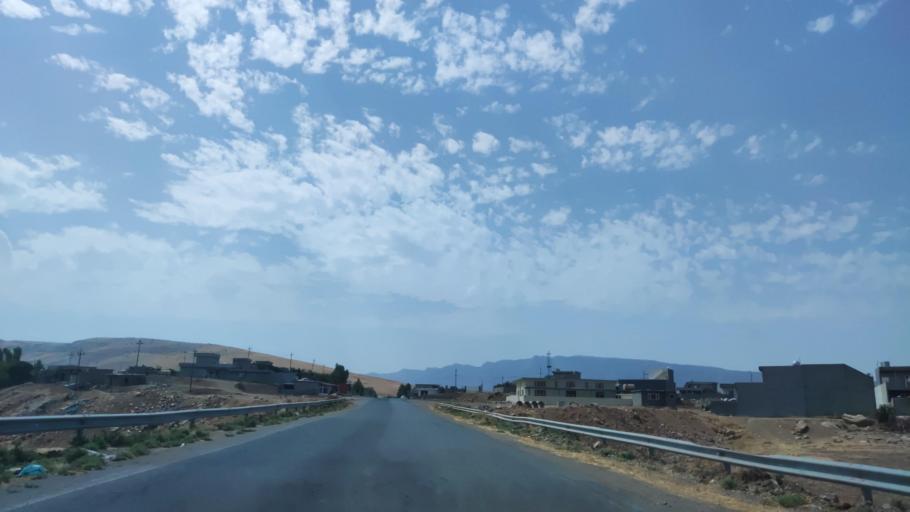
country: IQ
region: Arbil
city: Shaqlawah
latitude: 36.4801
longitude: 44.3977
